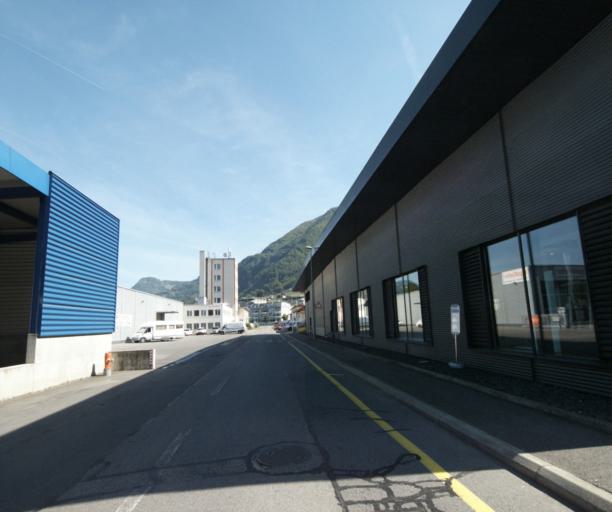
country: CH
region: Vaud
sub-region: Aigle District
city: Villeneuve
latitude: 46.3944
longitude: 6.9306
